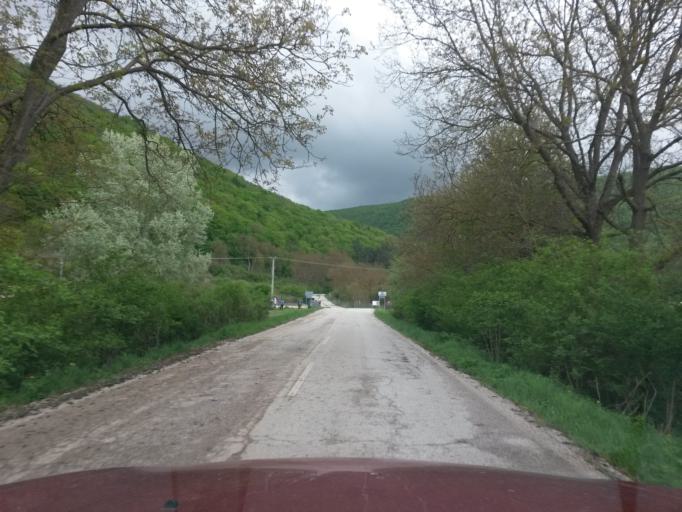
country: SK
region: Kosicky
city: Roznava
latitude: 48.5705
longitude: 20.4649
